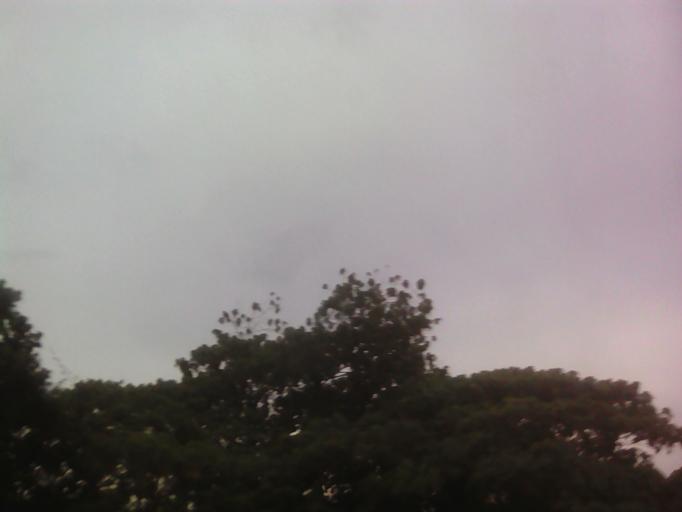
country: MY
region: Penang
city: Perai
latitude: 5.3978
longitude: 100.4136
